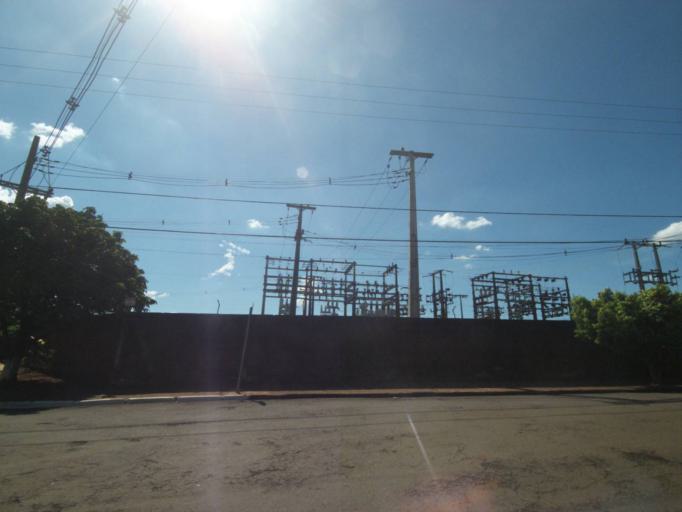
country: BR
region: Parana
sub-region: Sertanopolis
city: Sertanopolis
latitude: -23.0442
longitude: -50.8221
